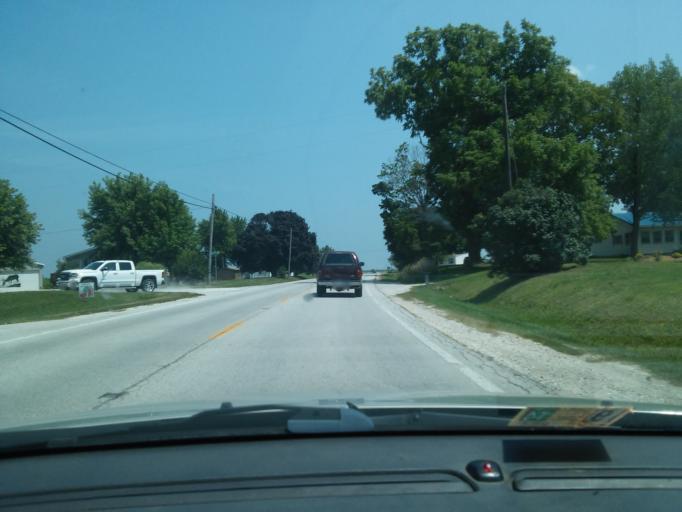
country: US
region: Illinois
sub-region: Pike County
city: Pittsfield
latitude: 39.5762
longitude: -90.9098
